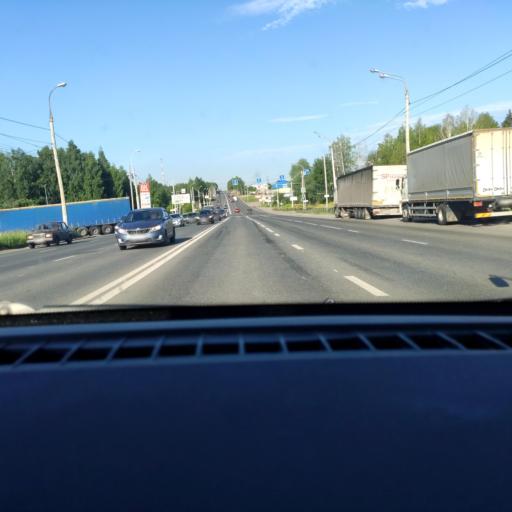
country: RU
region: Udmurtiya
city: Khokhryaki
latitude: 56.9046
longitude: 53.3374
